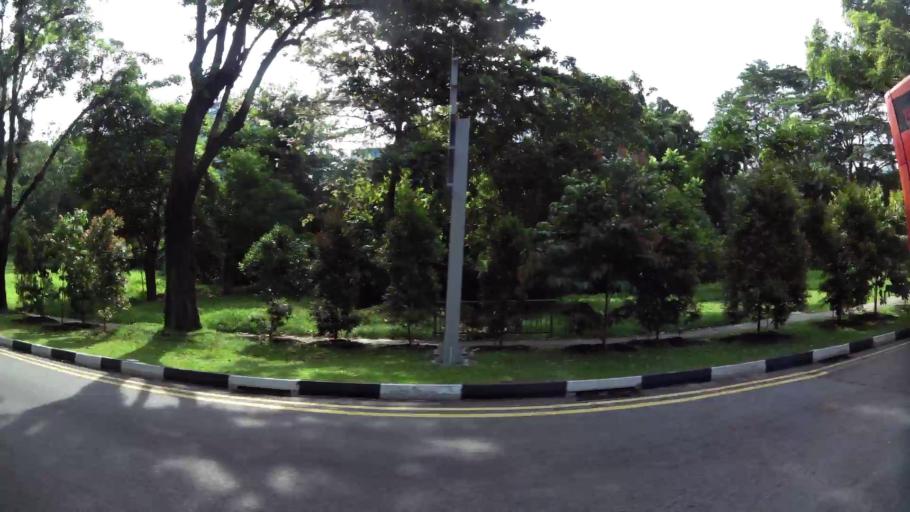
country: SG
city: Singapore
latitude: 1.3042
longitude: 103.7884
